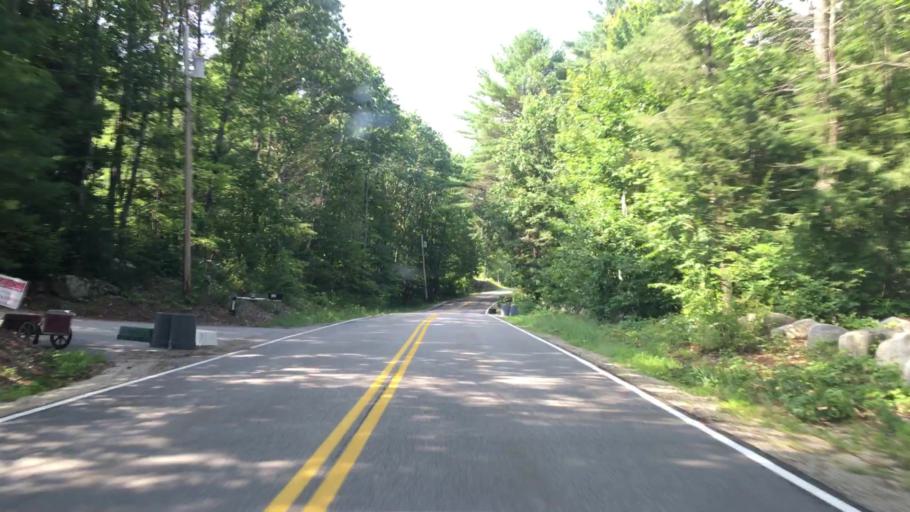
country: US
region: Maine
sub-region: Cumberland County
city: Raymond
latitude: 43.9565
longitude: -70.4207
